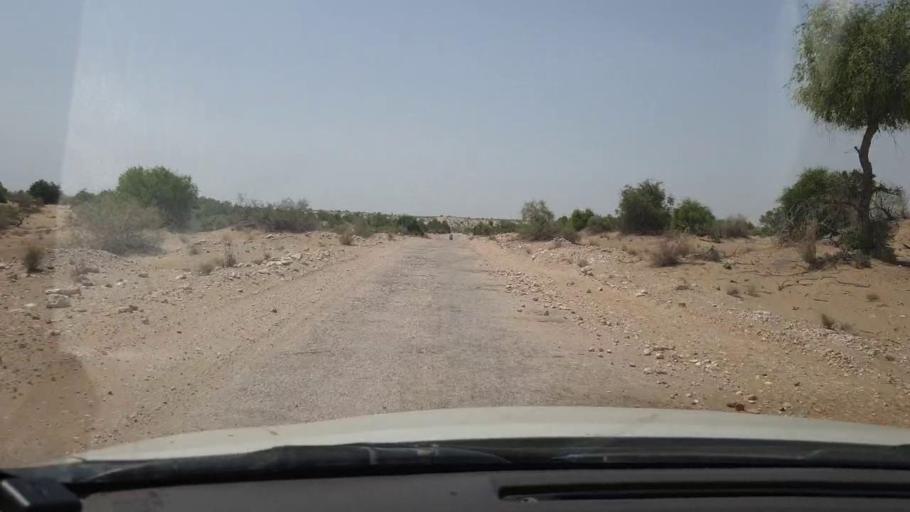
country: PK
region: Sindh
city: Rohri
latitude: 27.3135
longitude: 69.2817
